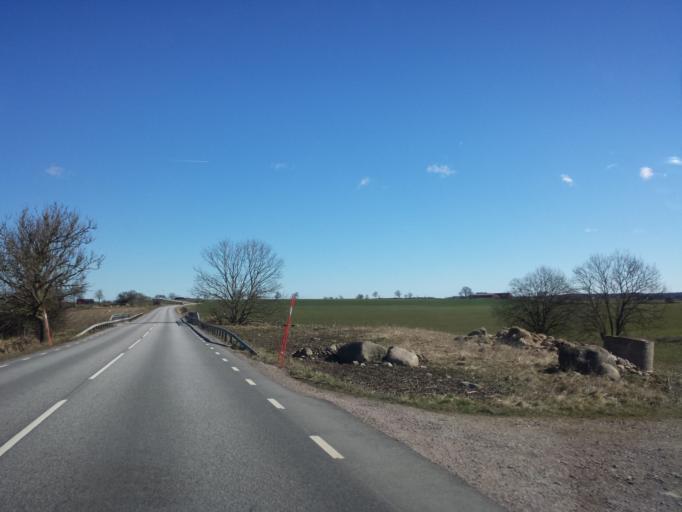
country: SE
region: Skane
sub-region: Tomelilla Kommun
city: Tomelilla
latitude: 55.6313
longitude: 13.8673
